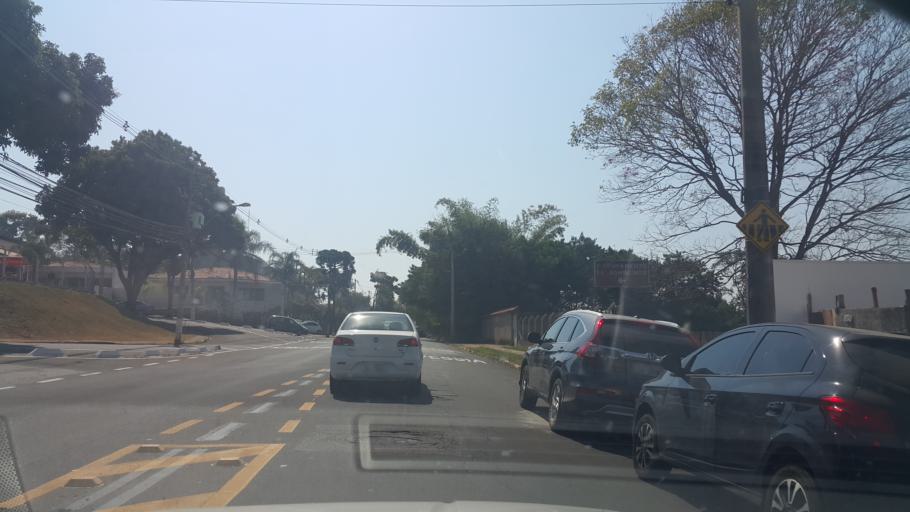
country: BR
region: Sao Paulo
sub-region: Campinas
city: Campinas
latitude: -22.8663
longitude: -47.0488
